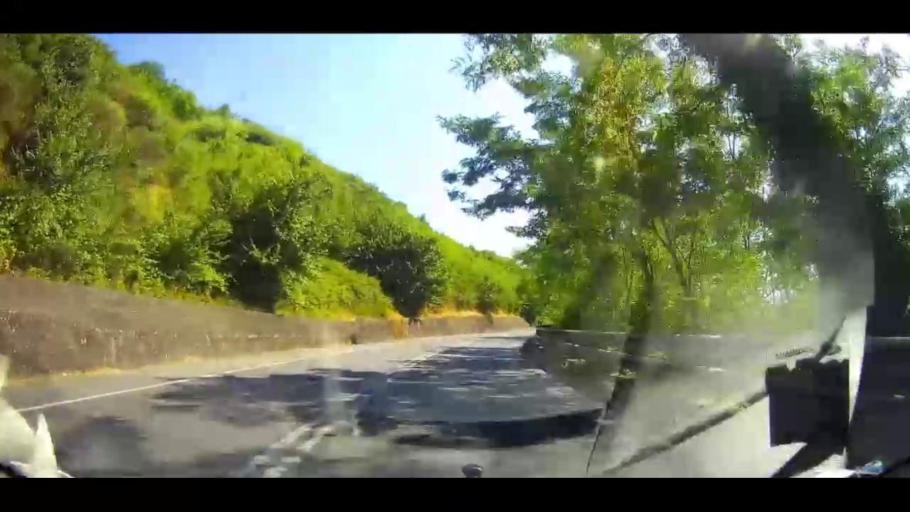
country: IT
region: Calabria
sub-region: Provincia di Cosenza
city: Cosenza
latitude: 39.3000
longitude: 16.2652
